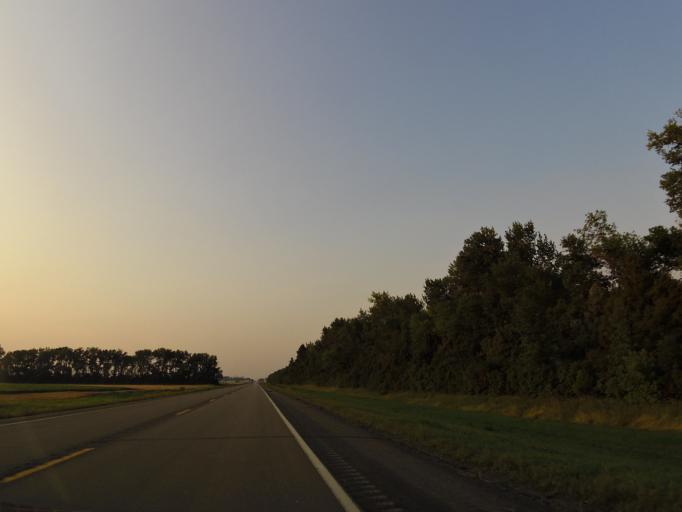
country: US
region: North Dakota
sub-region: Grand Forks County
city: Larimore
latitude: 47.8849
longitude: -97.6237
